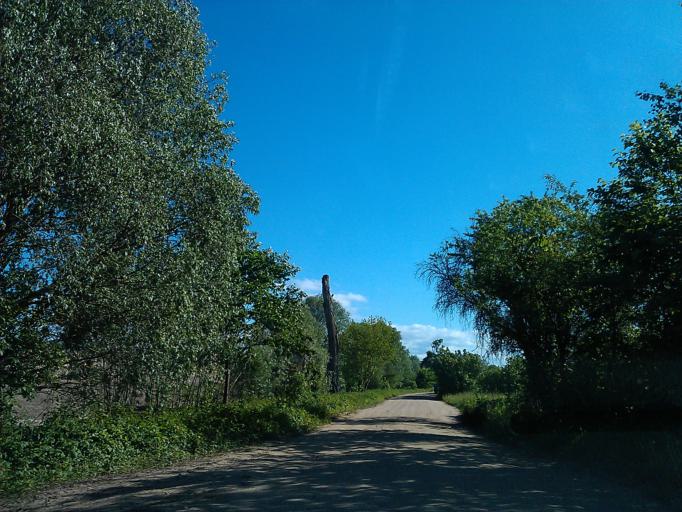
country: LV
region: Adazi
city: Adazi
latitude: 57.0905
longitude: 24.3220
